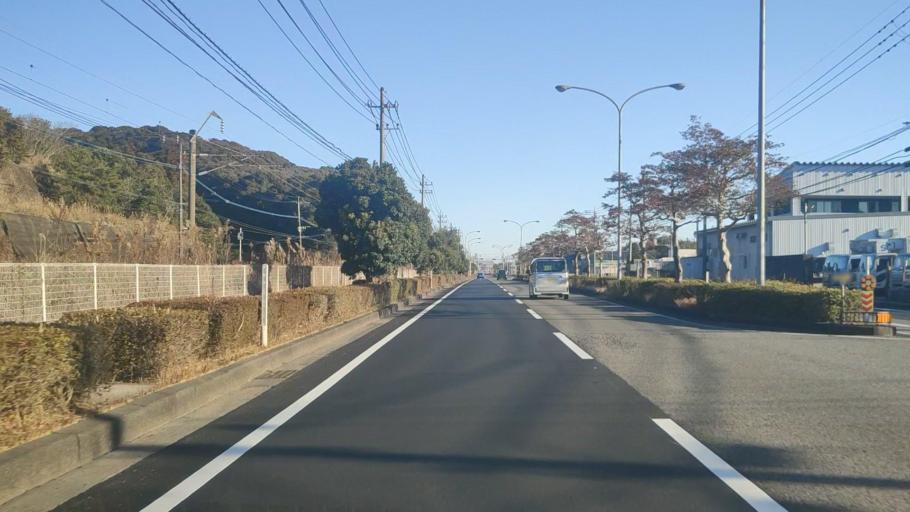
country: JP
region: Miyazaki
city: Nobeoka
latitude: 32.4520
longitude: 131.6410
